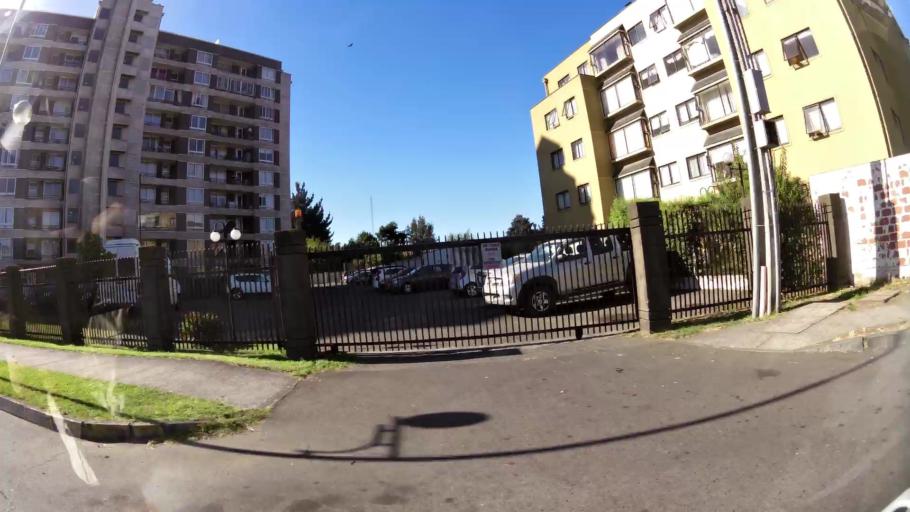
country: CL
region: Biobio
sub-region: Provincia de Concepcion
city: Concepcion
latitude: -36.8429
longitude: -73.1145
